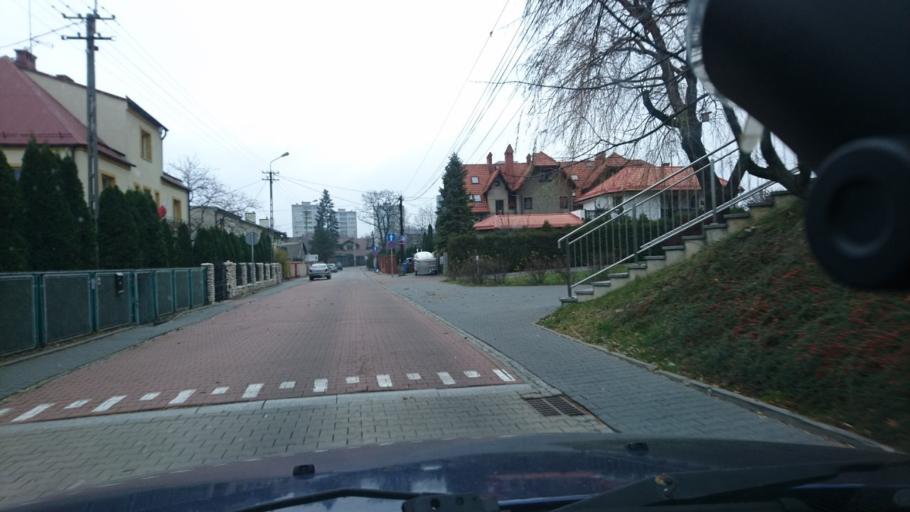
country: PL
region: Silesian Voivodeship
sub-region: Bielsko-Biala
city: Bielsko-Biala
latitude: 49.8127
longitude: 19.0167
